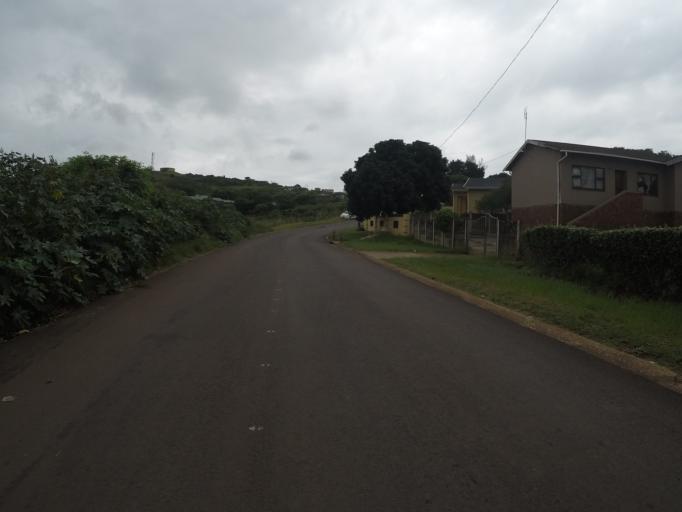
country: ZA
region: KwaZulu-Natal
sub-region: uThungulu District Municipality
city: Empangeni
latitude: -28.7733
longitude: 31.8605
